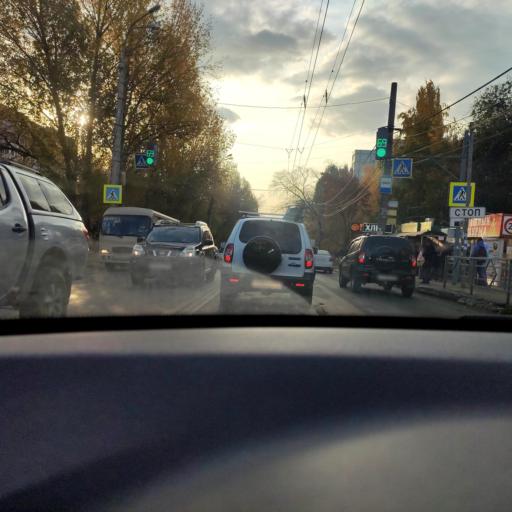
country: RU
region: Samara
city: Samara
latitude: 53.2431
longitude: 50.2326
